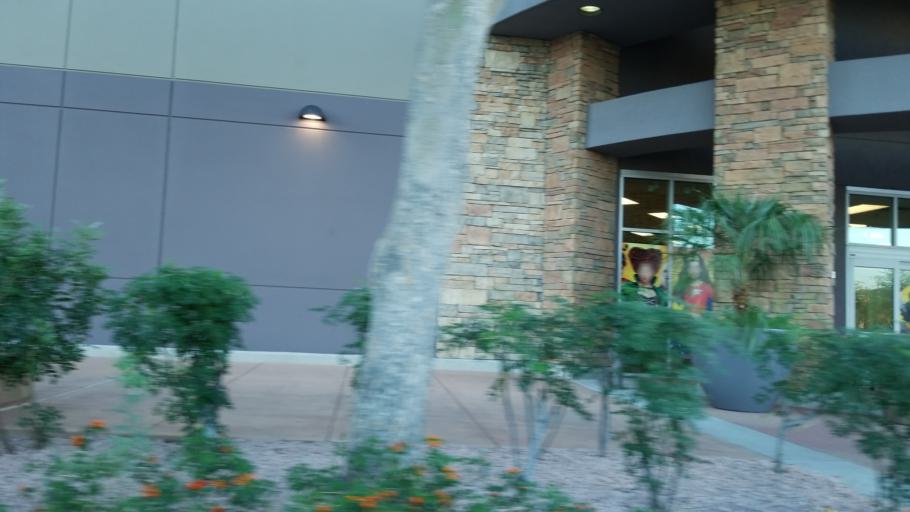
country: US
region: Arizona
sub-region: Maricopa County
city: Paradise Valley
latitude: 33.6744
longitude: -111.9722
